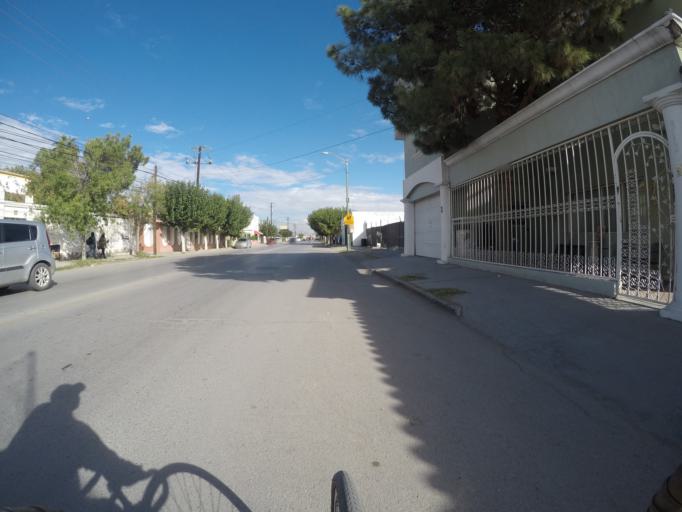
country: MX
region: Chihuahua
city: Ciudad Juarez
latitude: 31.7403
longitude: -106.4334
